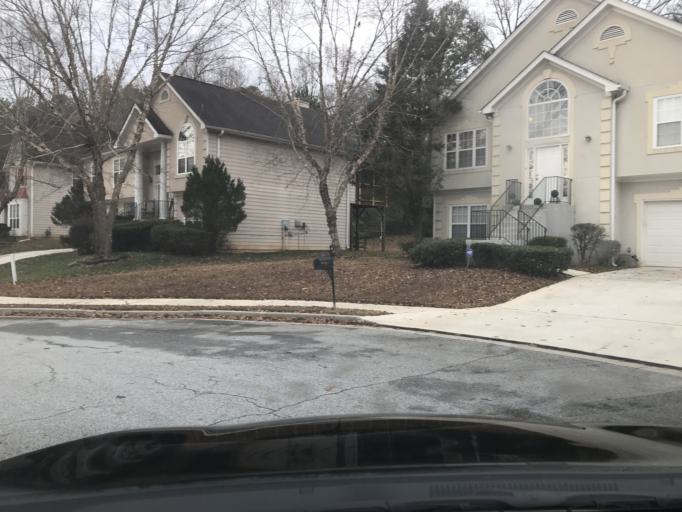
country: US
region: Georgia
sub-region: Fulton County
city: East Point
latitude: 33.7144
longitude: -84.5053
